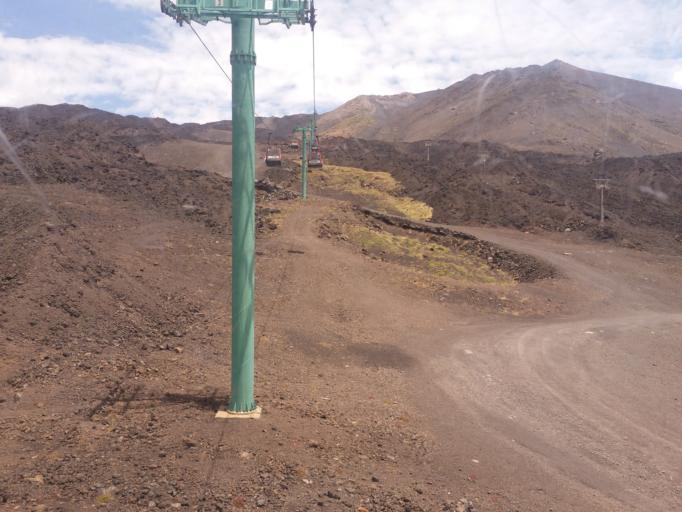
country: IT
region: Sicily
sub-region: Catania
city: Ragalna
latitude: 37.7021
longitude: 14.9991
